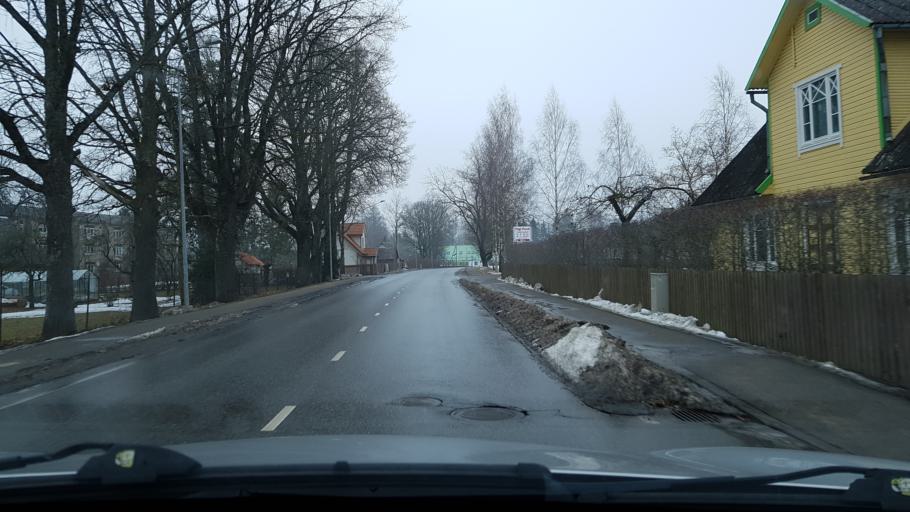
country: EE
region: Valgamaa
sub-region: Torva linn
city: Torva
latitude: 58.2342
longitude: 25.8766
